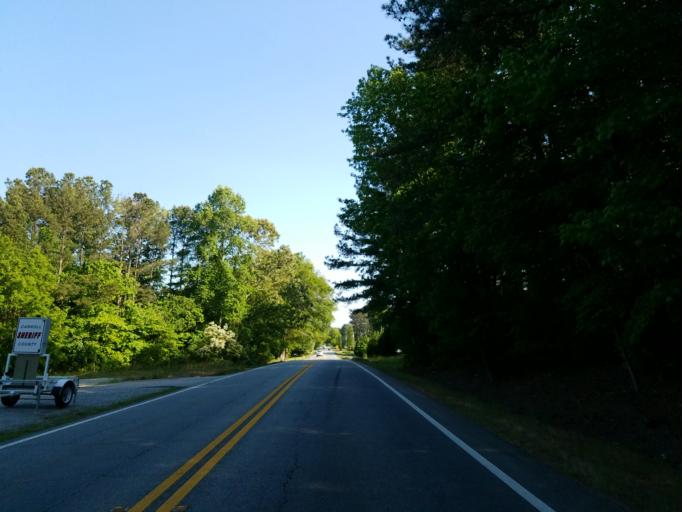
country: US
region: Georgia
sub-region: Carroll County
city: Villa Rica
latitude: 33.7879
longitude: -84.9683
